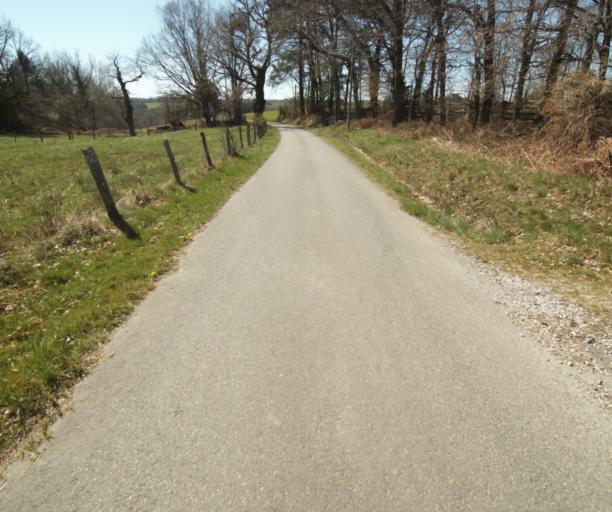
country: FR
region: Limousin
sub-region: Departement de la Correze
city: Chamboulive
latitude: 45.4596
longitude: 1.7098
